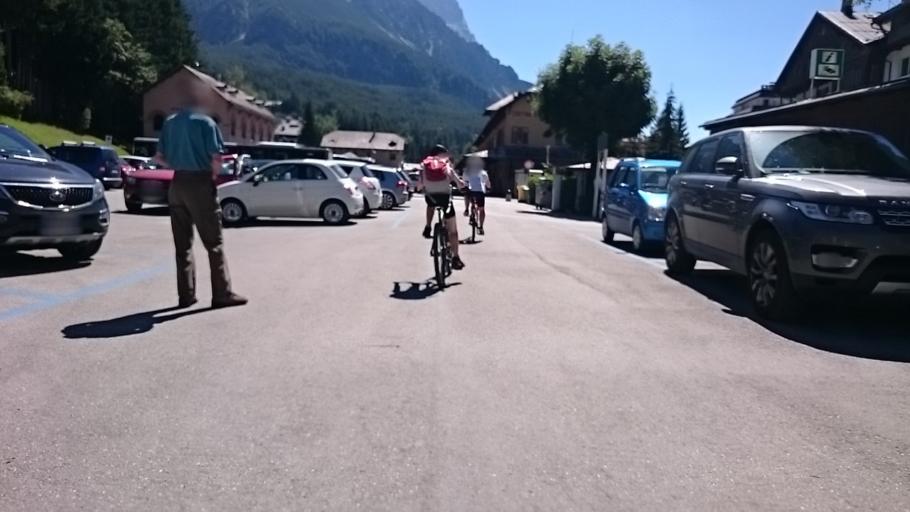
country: IT
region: Veneto
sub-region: Provincia di Belluno
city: Cortina d'Ampezzo
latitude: 46.5398
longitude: 12.1371
